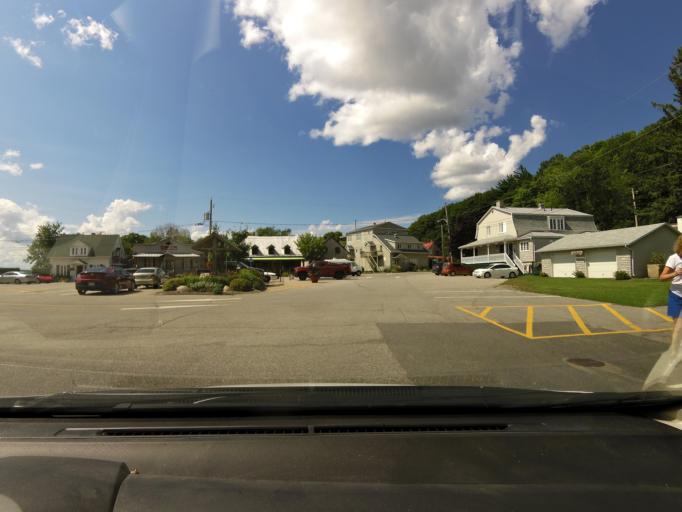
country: CA
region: Quebec
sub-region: Capitale-Nationale
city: Cap-Sante
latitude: 46.6710
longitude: -71.7875
